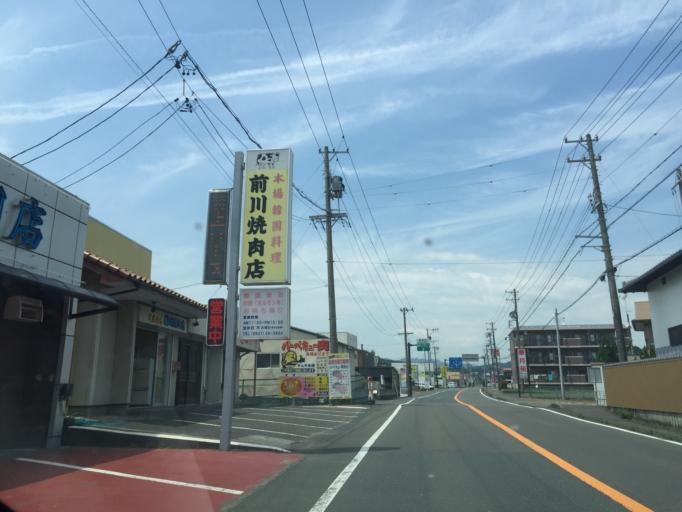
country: JP
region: Shizuoka
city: Mori
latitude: 34.8033
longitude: 137.9570
